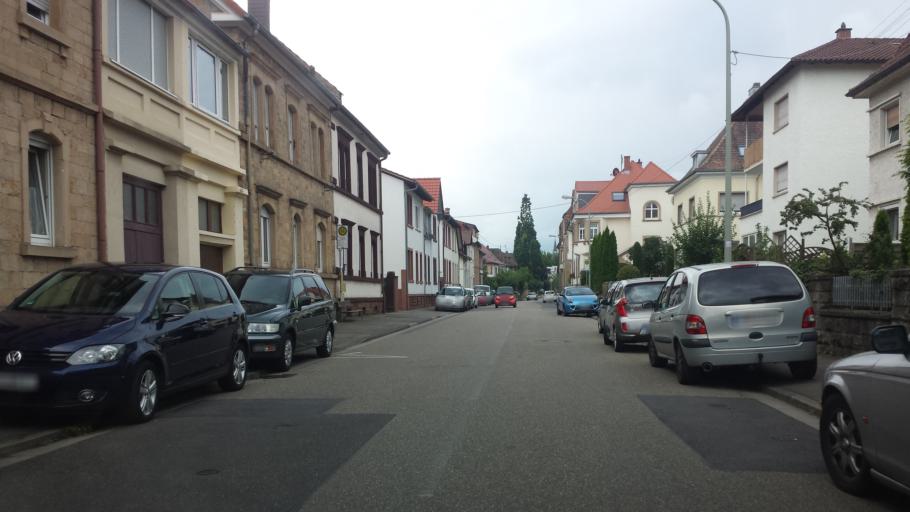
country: DE
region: Rheinland-Pfalz
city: Neustadt
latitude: 49.3433
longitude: 8.1360
